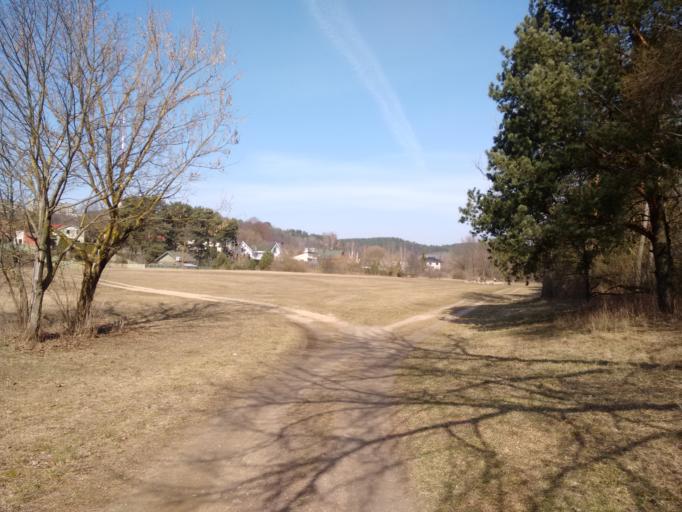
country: LT
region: Vilnius County
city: Vilkpede
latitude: 54.6783
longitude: 25.2302
